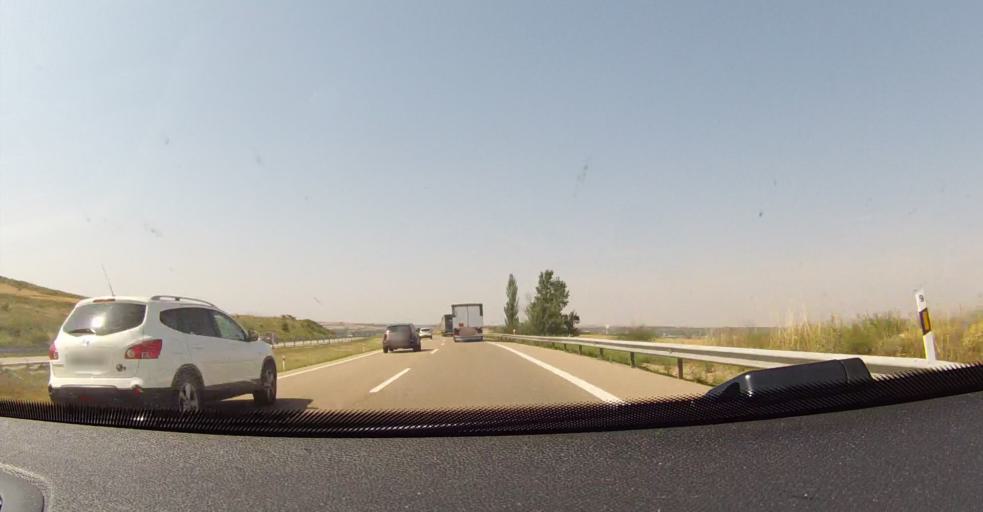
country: ES
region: Castille and Leon
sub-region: Provincia de Burgos
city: Cardenajimeno
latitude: 42.3556
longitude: -3.6010
